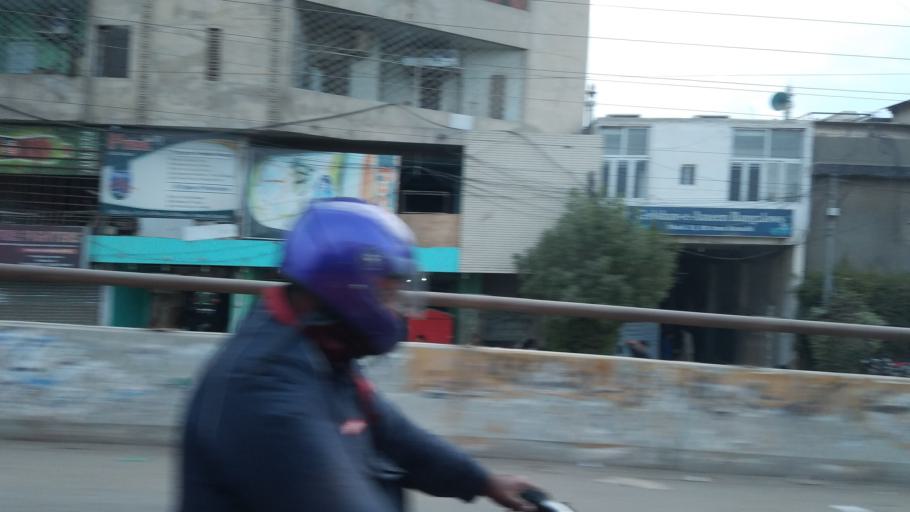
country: PK
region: Sindh
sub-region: Karachi District
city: Karachi
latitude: 24.9416
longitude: 67.0850
